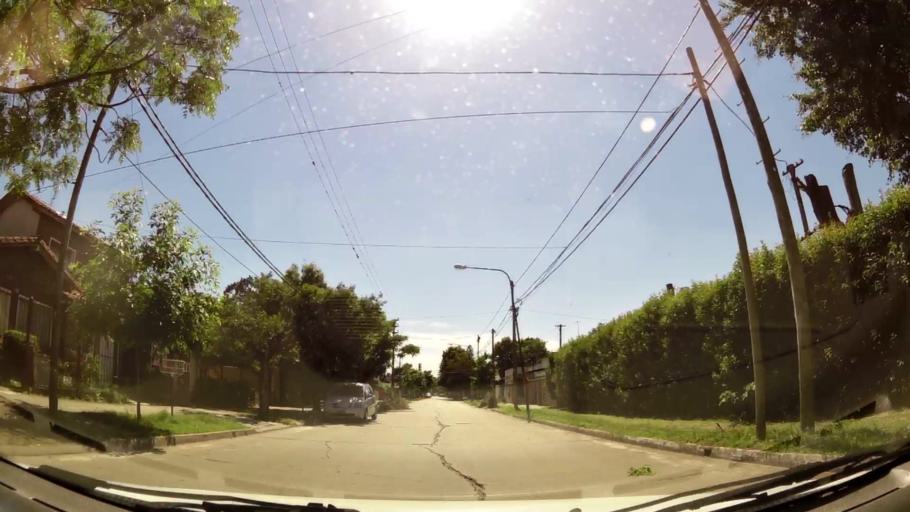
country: AR
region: Buenos Aires
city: Ituzaingo
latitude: -34.6626
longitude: -58.6651
